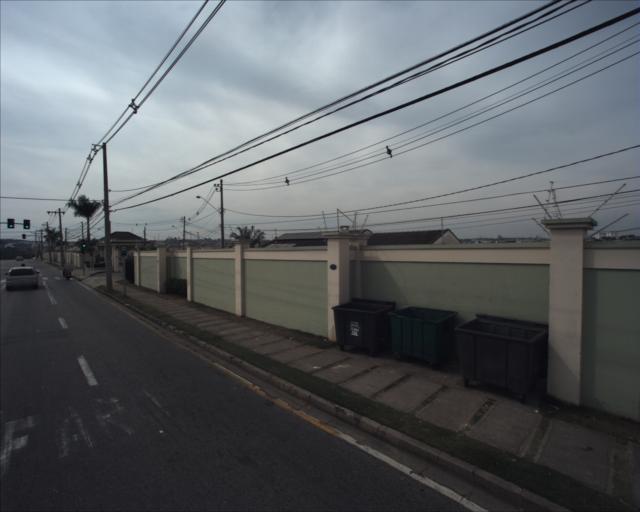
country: BR
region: Sao Paulo
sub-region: Sorocaba
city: Sorocaba
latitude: -23.4744
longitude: -47.4553
